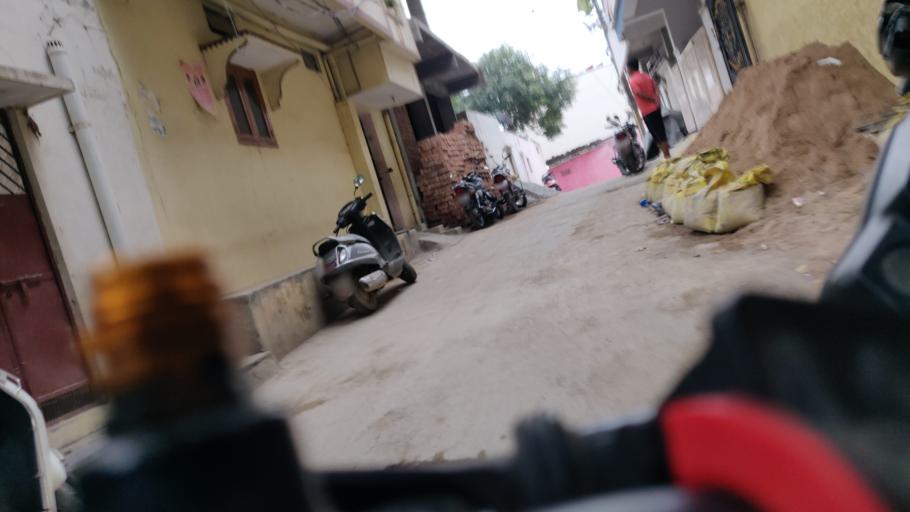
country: IN
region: Telangana
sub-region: Rangareddi
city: Kukatpalli
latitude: 17.4509
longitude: 78.4105
